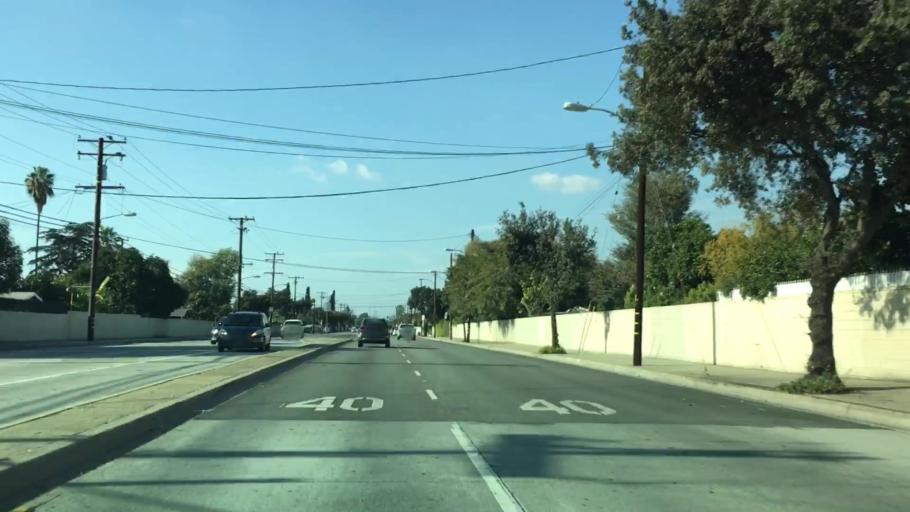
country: US
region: California
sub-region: Los Angeles County
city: West Puente Valley
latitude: 34.0547
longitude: -117.9783
